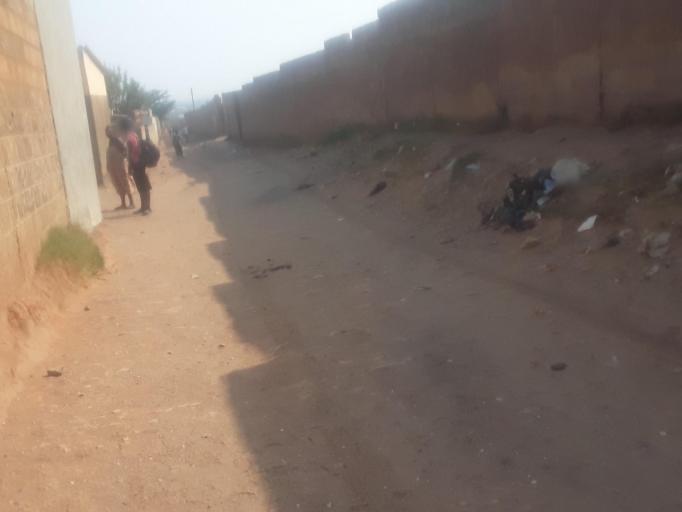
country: ZM
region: Lusaka
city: Lusaka
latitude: -15.3605
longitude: 28.2919
